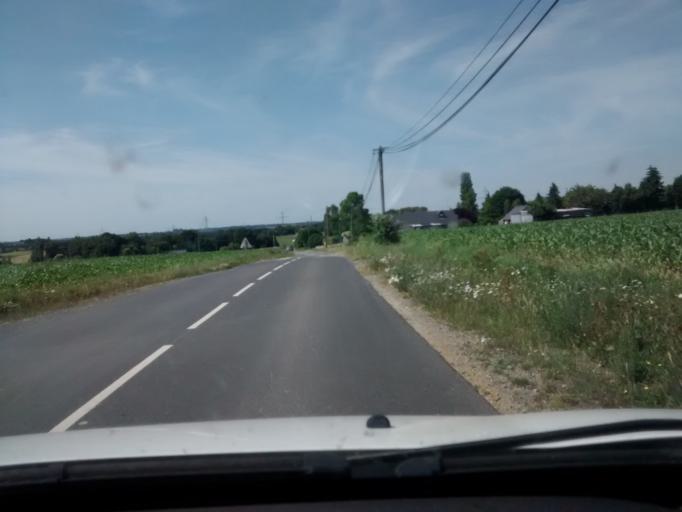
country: FR
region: Brittany
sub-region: Departement d'Ille-et-Vilaine
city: Acigne
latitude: 48.1004
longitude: -1.5649
